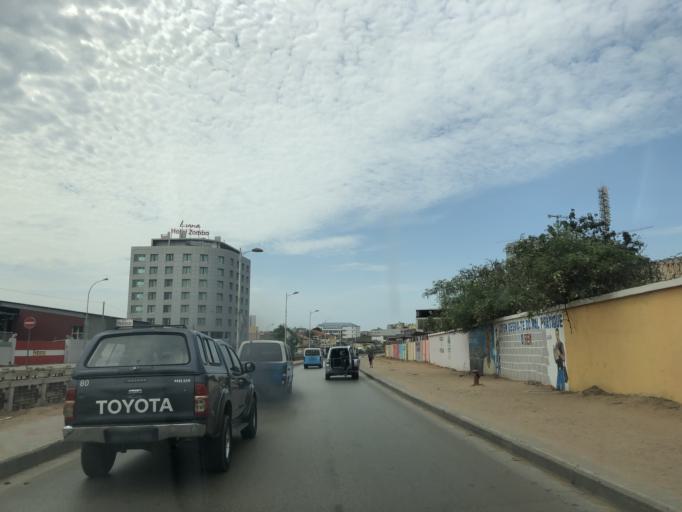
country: AO
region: Luanda
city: Luanda
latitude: -8.8295
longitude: 13.2550
